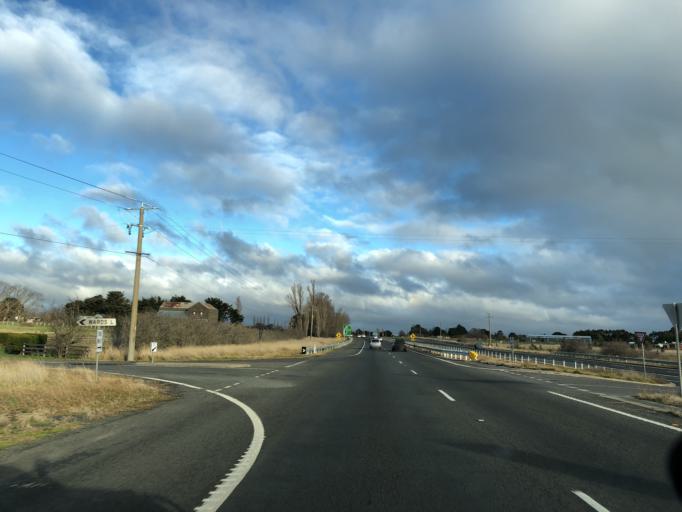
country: AU
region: Victoria
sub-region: Mount Alexander
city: Castlemaine
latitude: -37.2149
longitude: 144.4144
